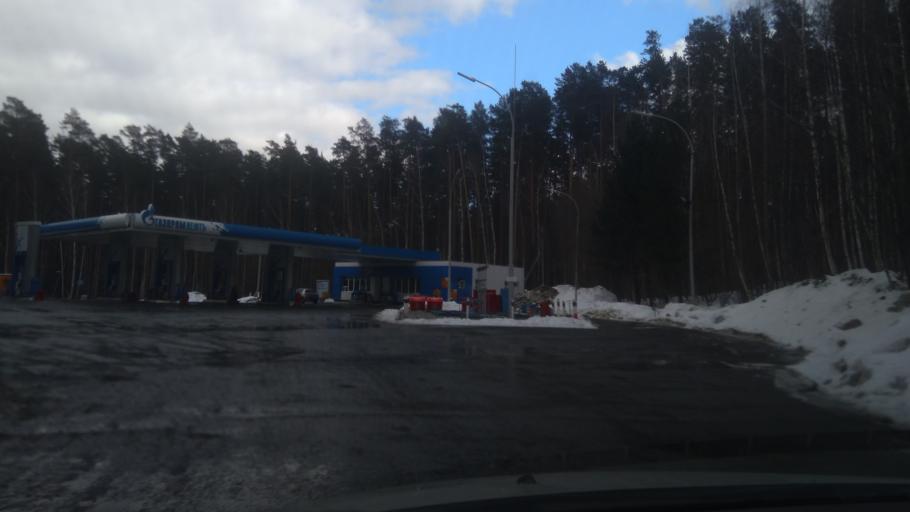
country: RU
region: Sverdlovsk
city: Shirokaya Rechka
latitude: 56.8248
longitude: 60.4672
